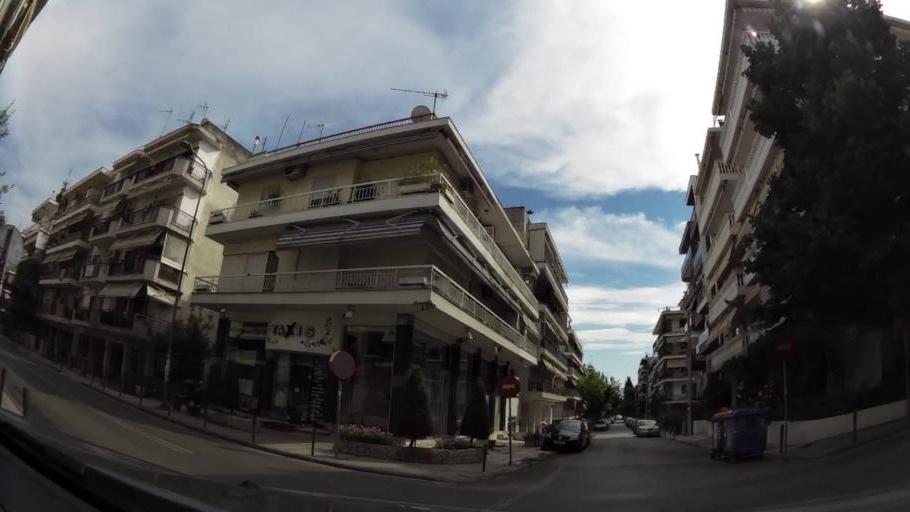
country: GR
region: Central Macedonia
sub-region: Nomos Thessalonikis
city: Kalamaria
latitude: 40.5758
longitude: 22.9503
